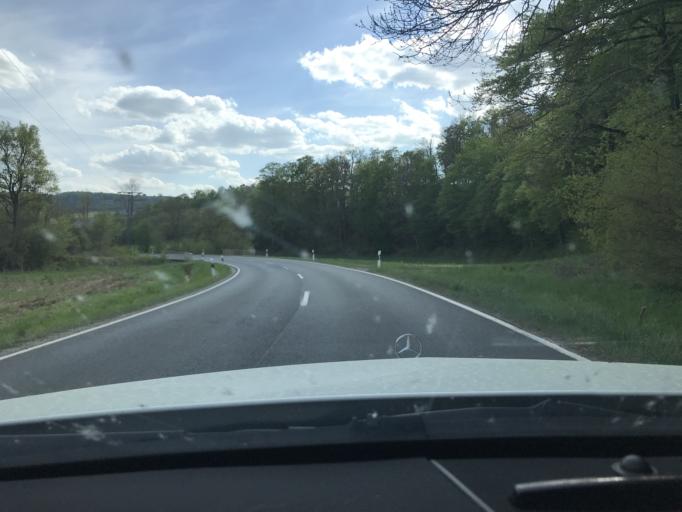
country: DE
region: Hesse
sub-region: Regierungsbezirk Kassel
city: Weissenborn
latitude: 51.1139
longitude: 10.0545
